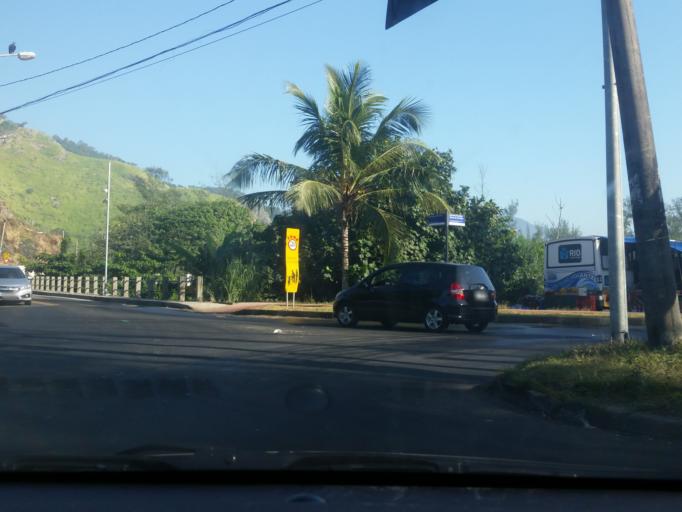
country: BR
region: Rio de Janeiro
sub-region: Nilopolis
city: Nilopolis
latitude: -23.0335
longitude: -43.4920
